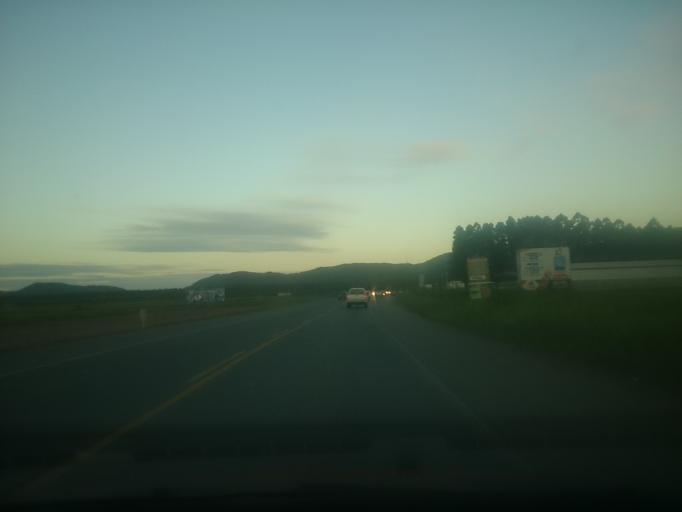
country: BR
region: Santa Catarina
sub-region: Navegantes
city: Navegantes
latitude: -26.8331
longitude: -48.7279
